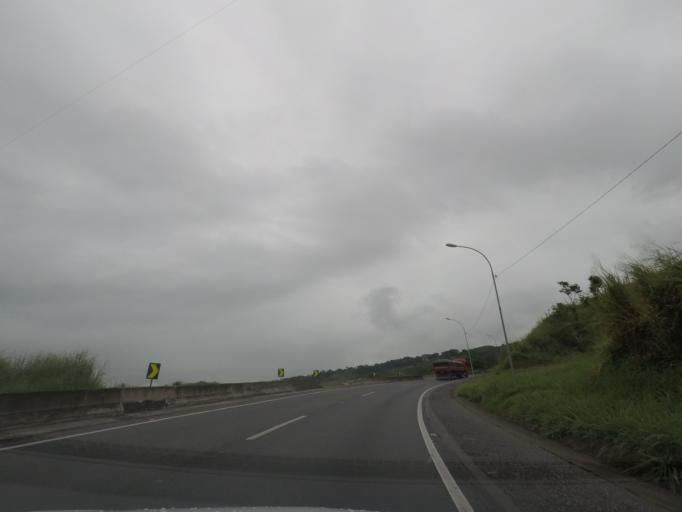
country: BR
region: Sao Paulo
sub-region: Cajati
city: Cajati
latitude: -24.8320
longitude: -48.2143
